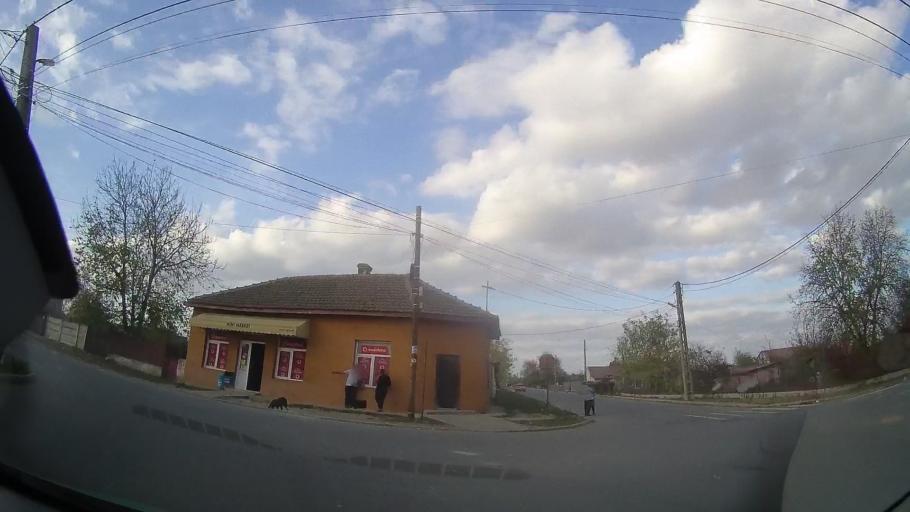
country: RO
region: Constanta
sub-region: Comuna Negru Voda
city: Negru Voda
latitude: 43.8178
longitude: 28.2086
